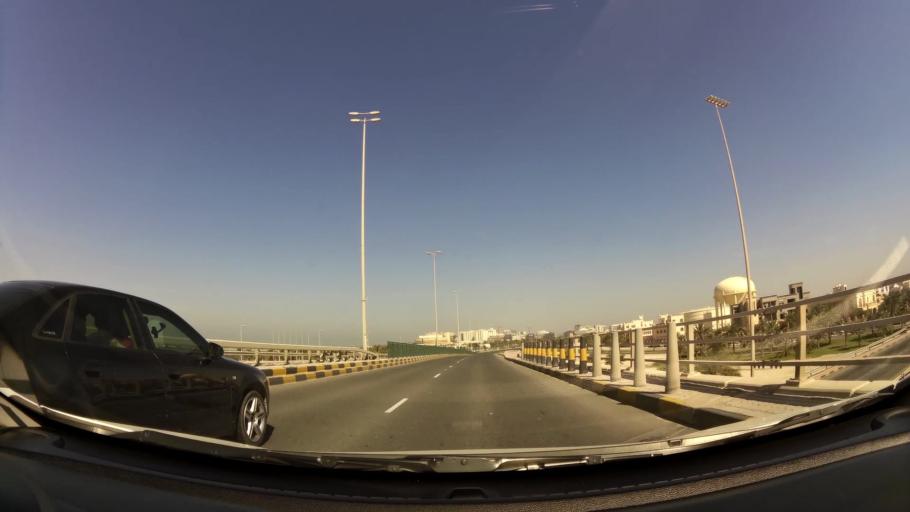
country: BH
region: Muharraq
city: Al Muharraq
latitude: 26.2512
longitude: 50.6050
